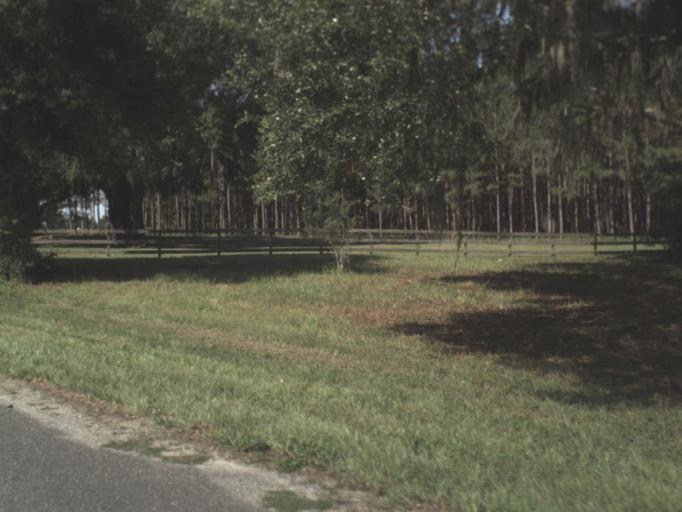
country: US
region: Florida
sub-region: Alachua County
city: High Springs
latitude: 29.9531
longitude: -82.7132
